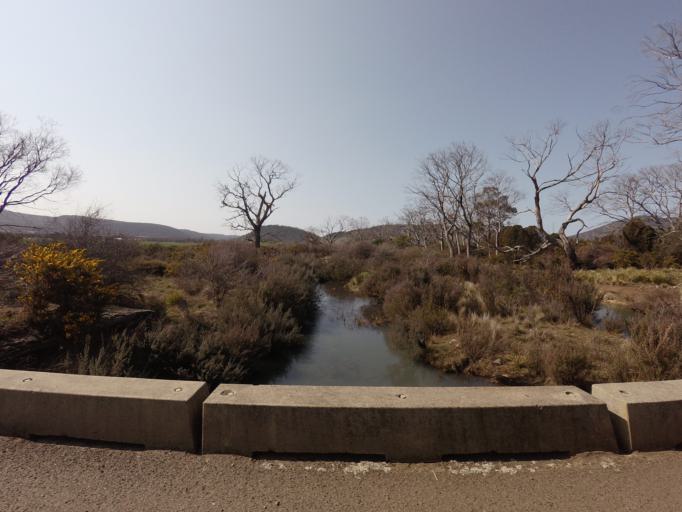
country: AU
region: Tasmania
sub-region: Break O'Day
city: St Helens
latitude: -41.8145
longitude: 147.9413
